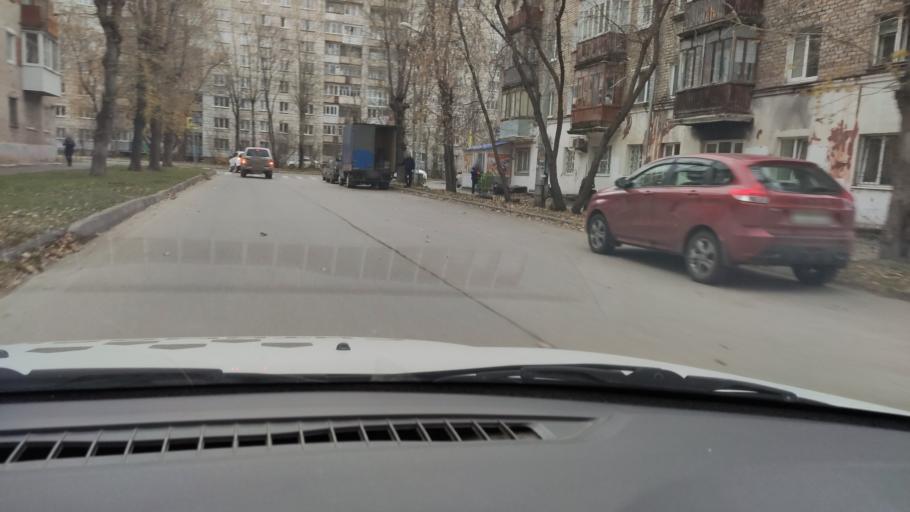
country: RU
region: Perm
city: Perm
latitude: 58.0182
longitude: 56.2849
